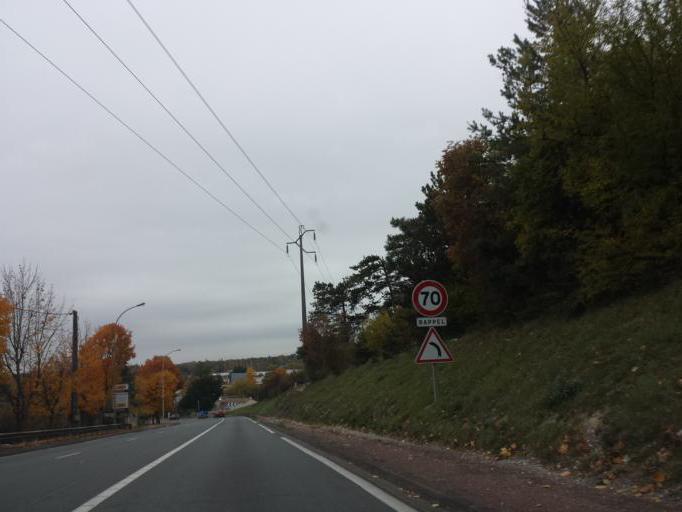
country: FR
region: Poitou-Charentes
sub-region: Departement de la Charente
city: Angouleme
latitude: 45.6331
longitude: 0.1316
